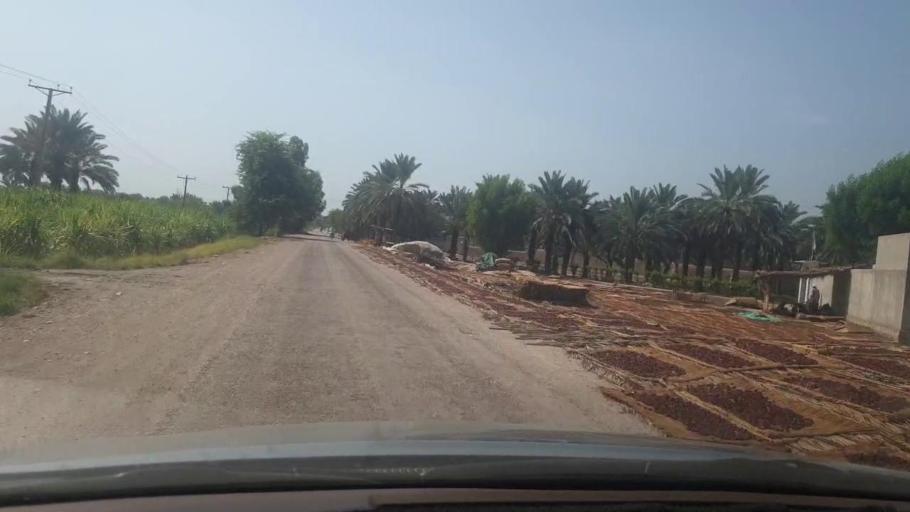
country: PK
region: Sindh
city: Ranipur
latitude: 27.2872
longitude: 68.5780
